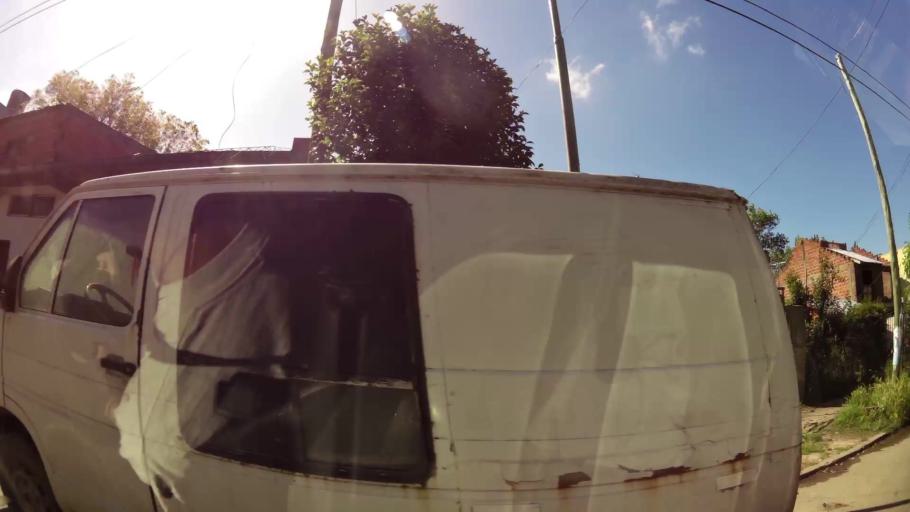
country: AR
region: Buenos Aires
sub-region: Partido de Quilmes
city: Quilmes
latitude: -34.7971
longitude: -58.2543
